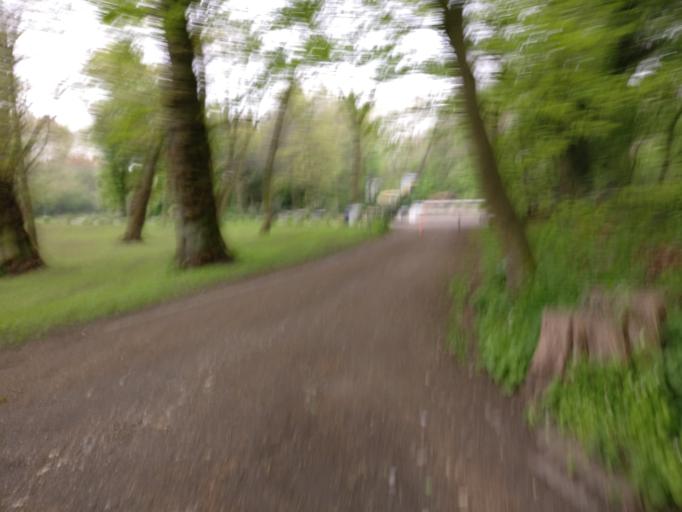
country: DE
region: North Rhine-Westphalia
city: Meiderich
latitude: 51.4880
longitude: 6.7613
